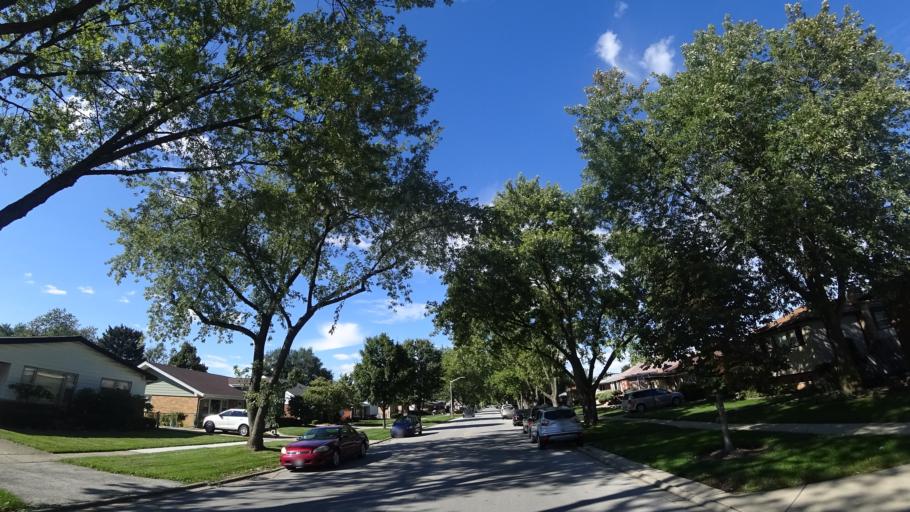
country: US
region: Illinois
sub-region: Cook County
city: Oak Lawn
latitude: 41.7057
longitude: -87.7500
